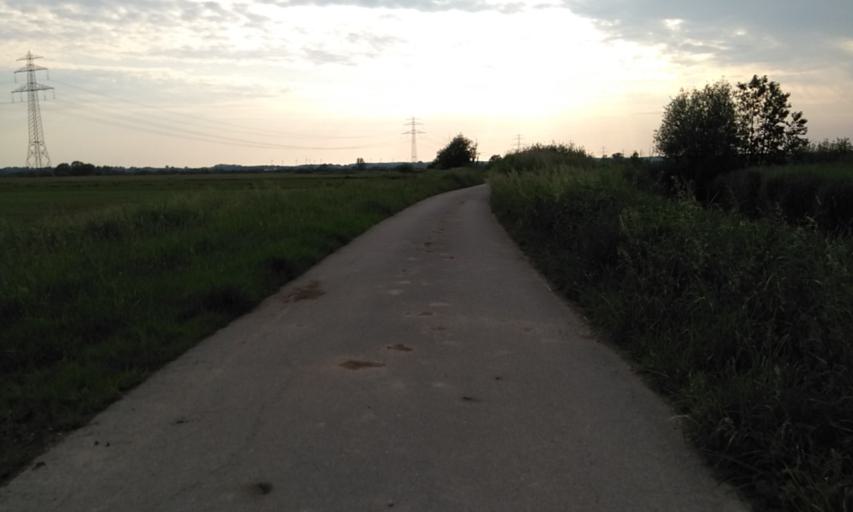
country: DE
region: Lower Saxony
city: Neuenkirchen
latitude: 53.5093
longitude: 9.6304
